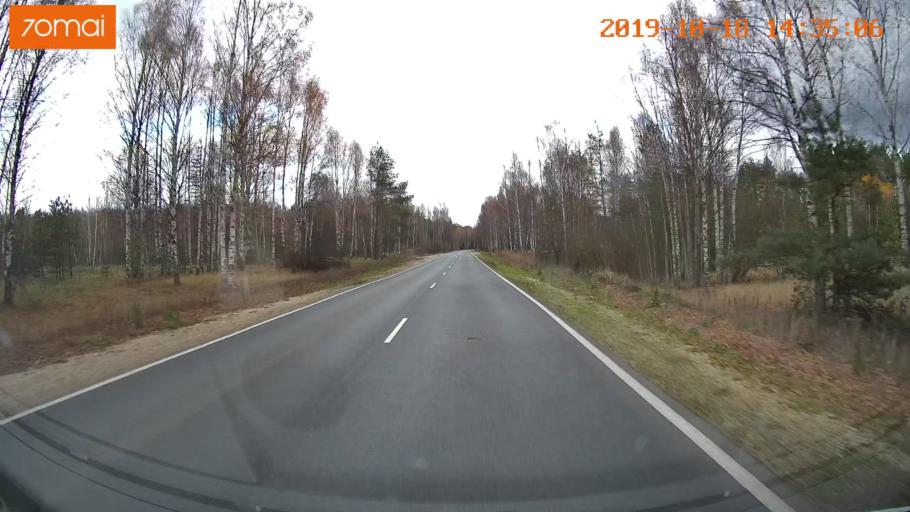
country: RU
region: Vladimir
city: Velikodvorskiy
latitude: 55.2196
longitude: 40.6296
